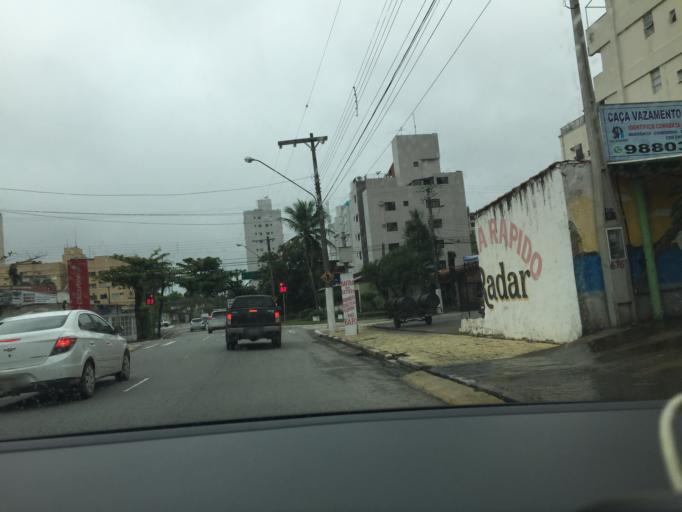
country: BR
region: Sao Paulo
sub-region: Guaruja
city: Guaruja
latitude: -23.9794
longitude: -46.2232
